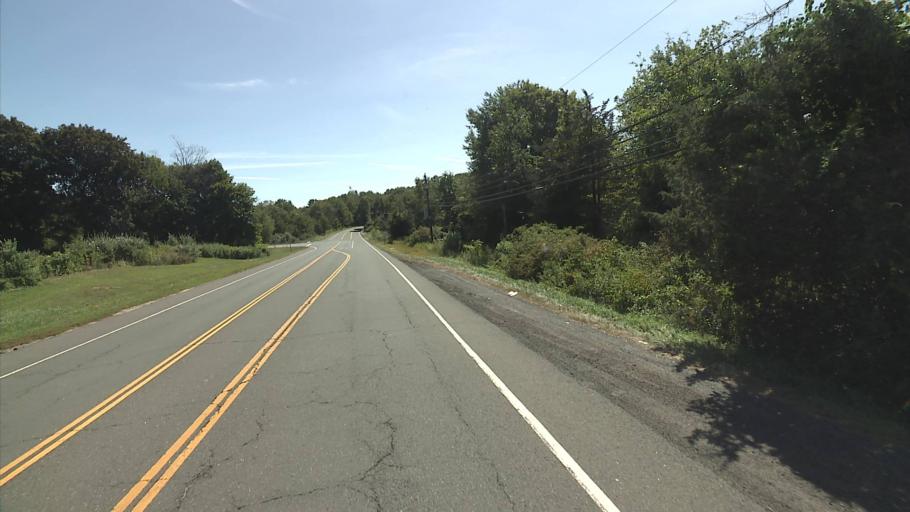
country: US
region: Connecticut
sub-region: New Haven County
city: Southbury
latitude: 41.4807
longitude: -73.1582
